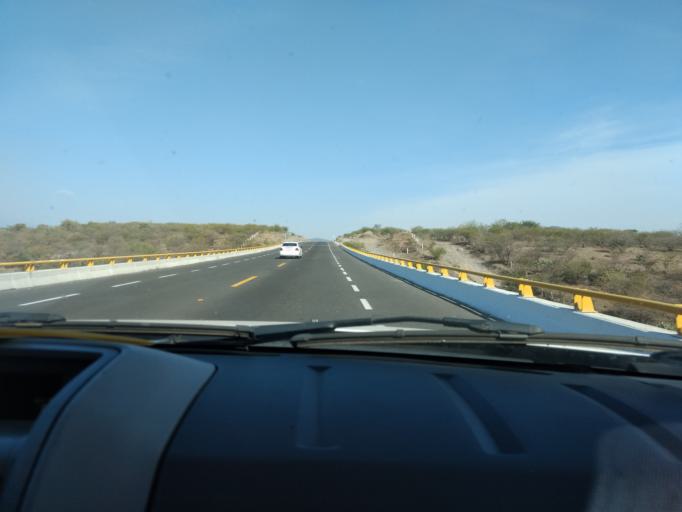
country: MX
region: Morelos
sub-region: Ayala
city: El Salitre
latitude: 18.6673
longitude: -98.9652
